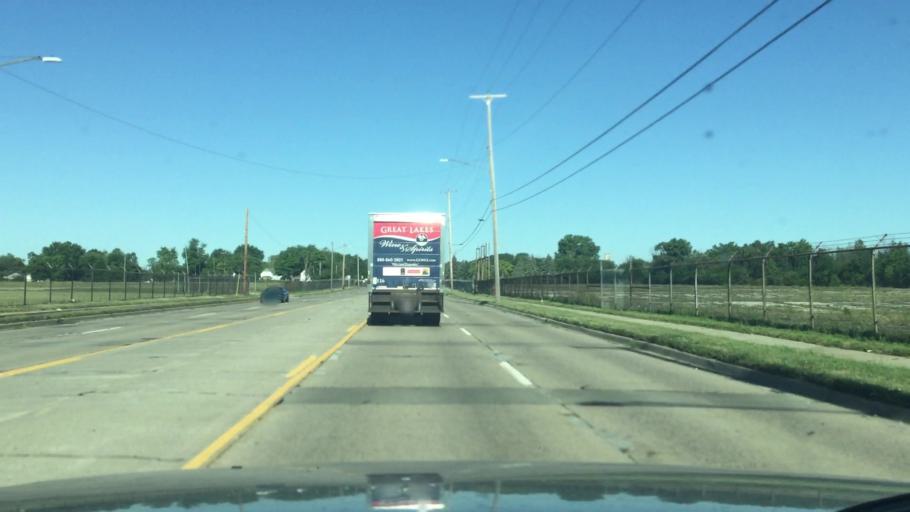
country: US
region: Michigan
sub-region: Saginaw County
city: Saginaw
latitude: 43.4101
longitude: -83.9458
